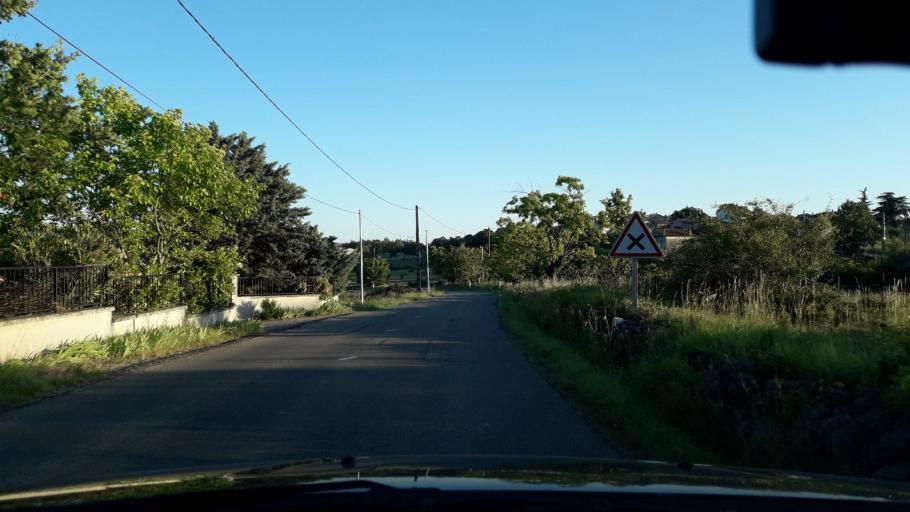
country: FR
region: Rhone-Alpes
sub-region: Departement de l'Ardeche
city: Lavilledieu
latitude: 44.5926
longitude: 4.4599
